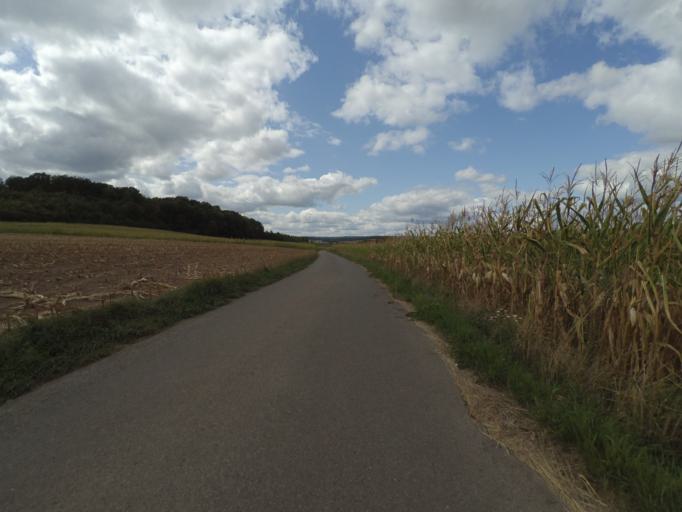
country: LU
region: Grevenmacher
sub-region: Canton de Grevenmacher
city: Betzdorf
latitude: 49.6855
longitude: 6.3369
